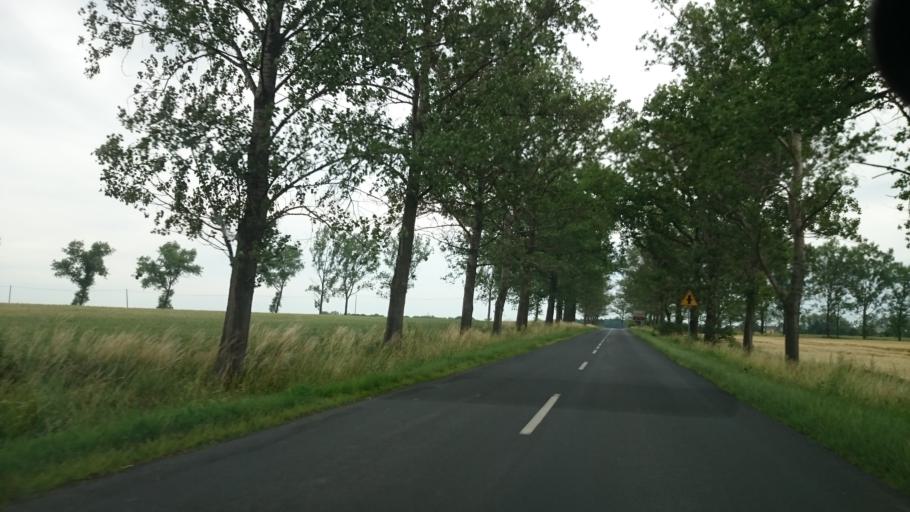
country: PL
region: Opole Voivodeship
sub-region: Powiat brzeski
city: Grodkow
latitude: 50.6774
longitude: 17.3145
